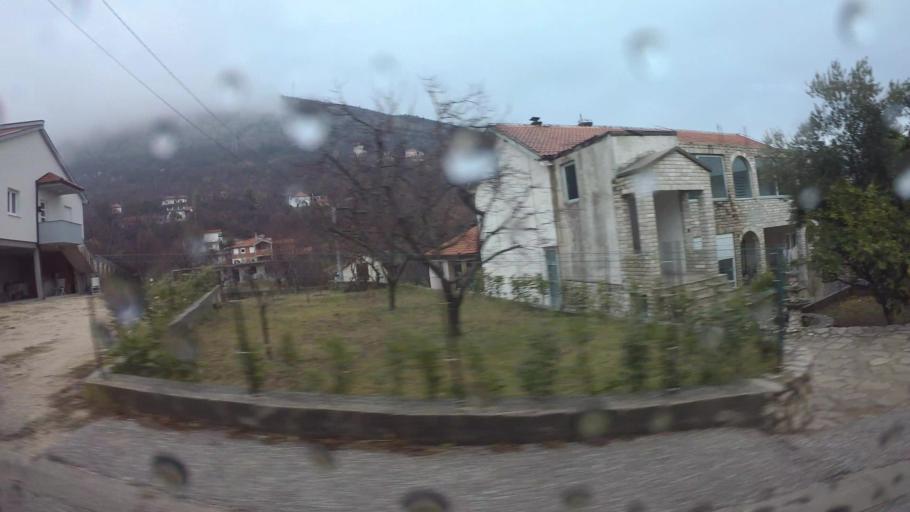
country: BA
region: Federation of Bosnia and Herzegovina
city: Cim
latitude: 43.3551
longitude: 17.7751
